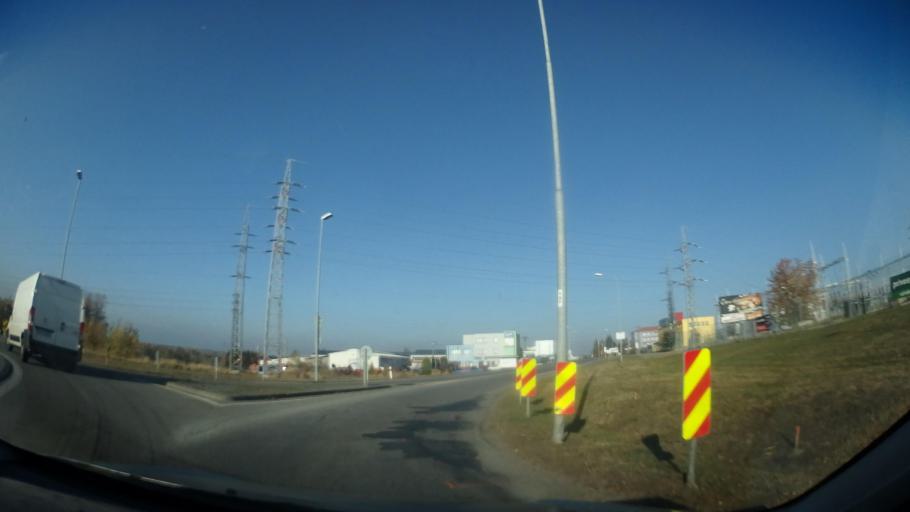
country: CZ
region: Vysocina
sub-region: Okres Zd'ar nad Sazavou
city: Zd'ar nad Sazavou
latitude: 49.5513
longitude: 15.9548
